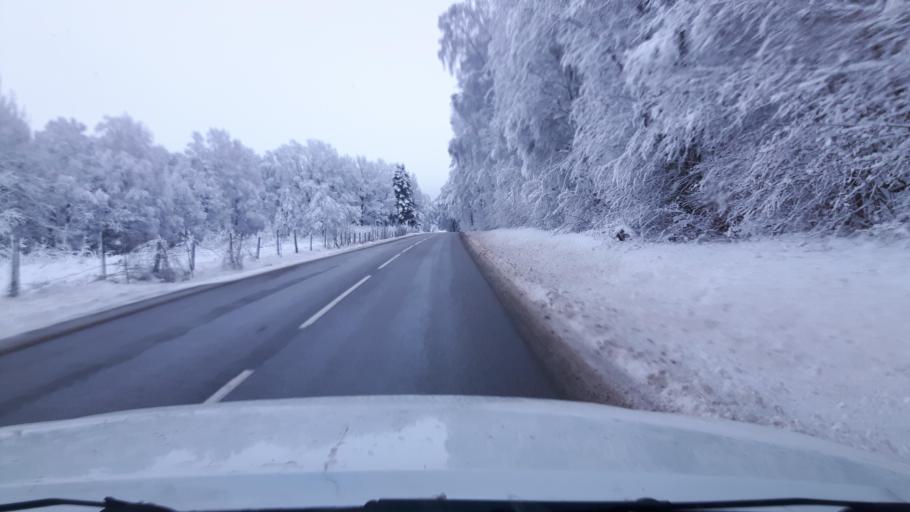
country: SE
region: Halland
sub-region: Kungsbacka Kommun
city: Fjaeras kyrkby
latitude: 57.4347
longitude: 12.1807
